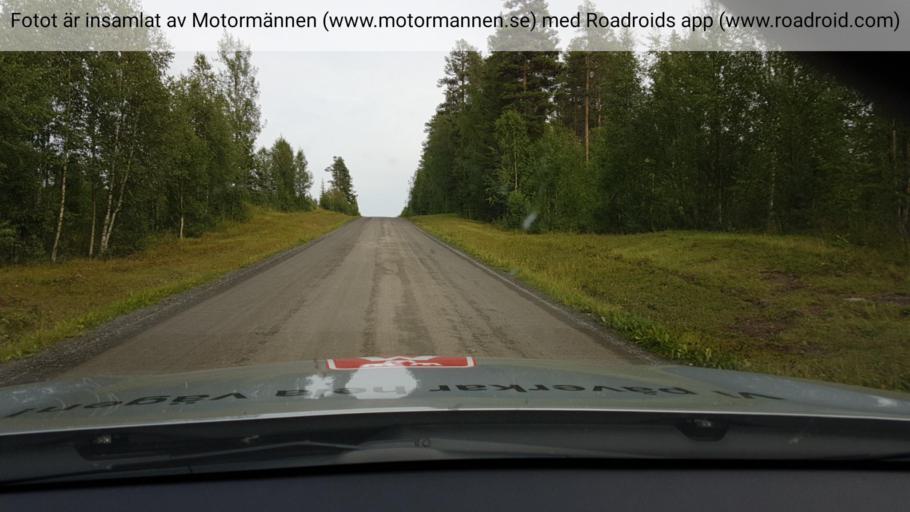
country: SE
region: Jaemtland
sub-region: OEstersunds Kommun
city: Lit
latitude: 63.6788
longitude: 14.8020
